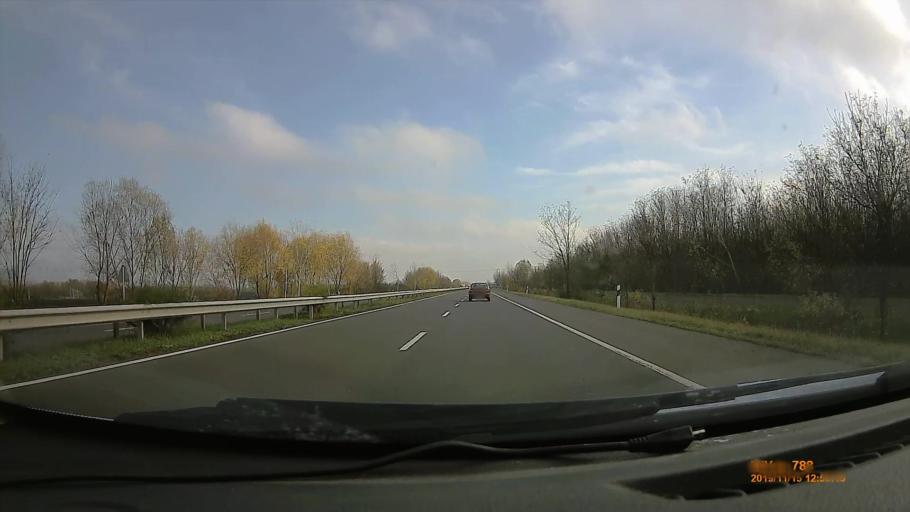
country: HU
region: Bekes
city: Bekescsaba
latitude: 46.6690
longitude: 21.1874
